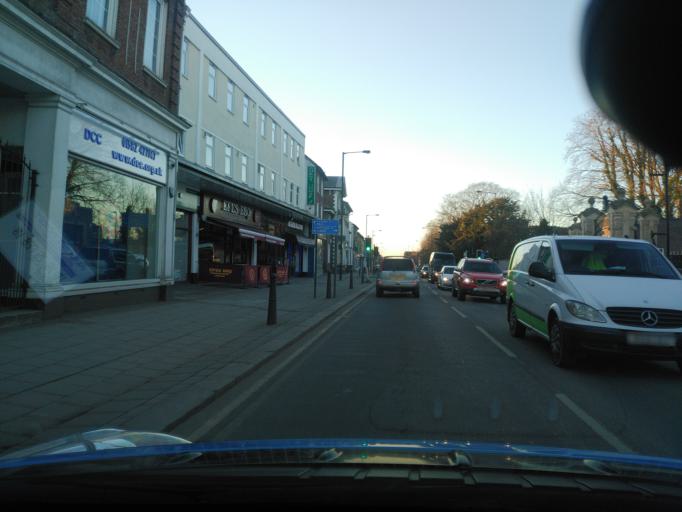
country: GB
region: England
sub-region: Central Bedfordshire
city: Dunstable
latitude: 51.8883
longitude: -0.5240
